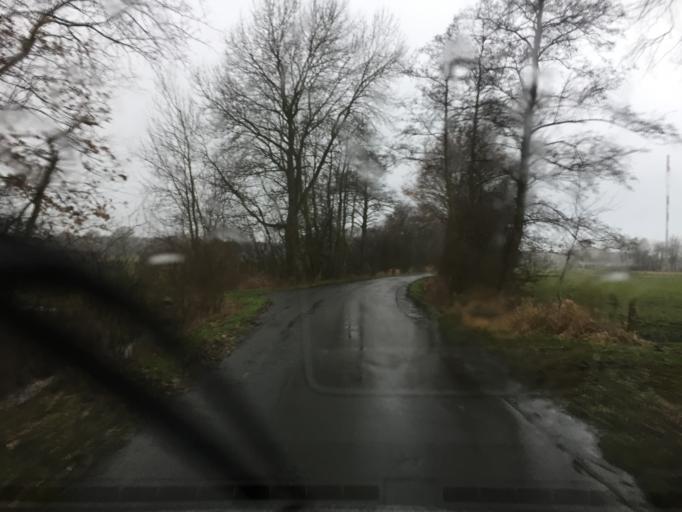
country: DE
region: Lower Saxony
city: Maasen
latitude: 52.6488
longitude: 8.8798
